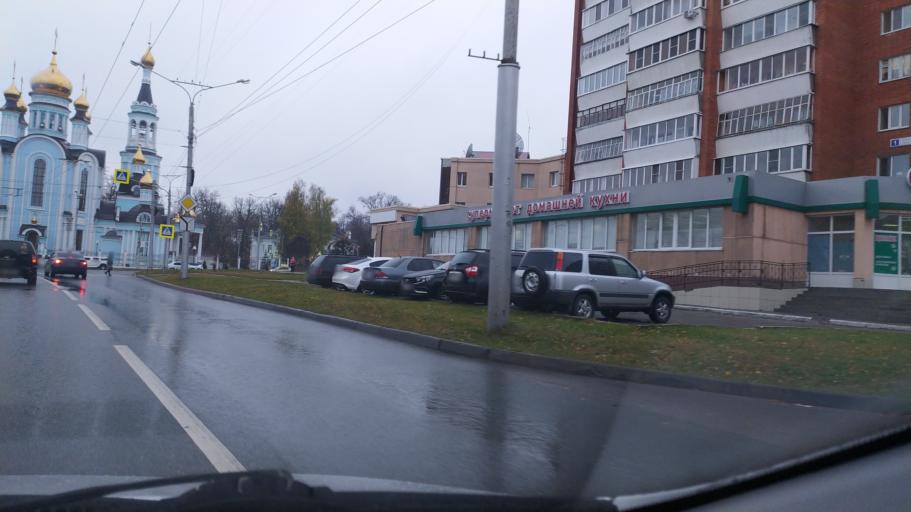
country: RU
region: Chuvashia
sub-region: Cheboksarskiy Rayon
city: Cheboksary
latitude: 56.1418
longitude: 47.1860
